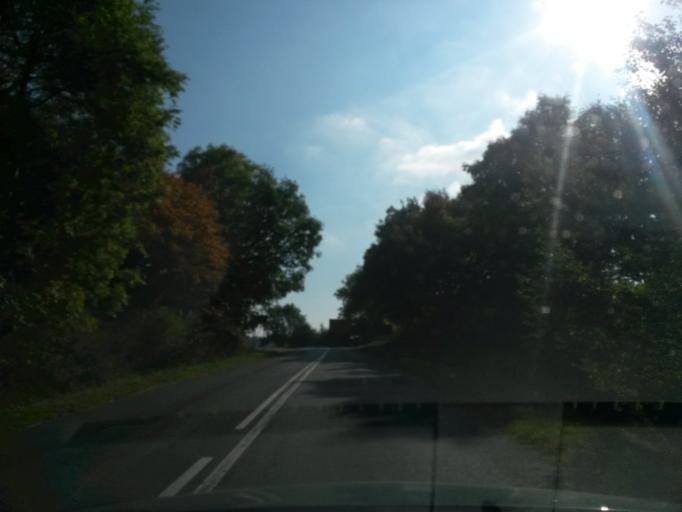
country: PL
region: Lower Silesian Voivodeship
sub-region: Powiat jeleniogorski
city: Kowary
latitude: 50.7633
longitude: 15.8667
